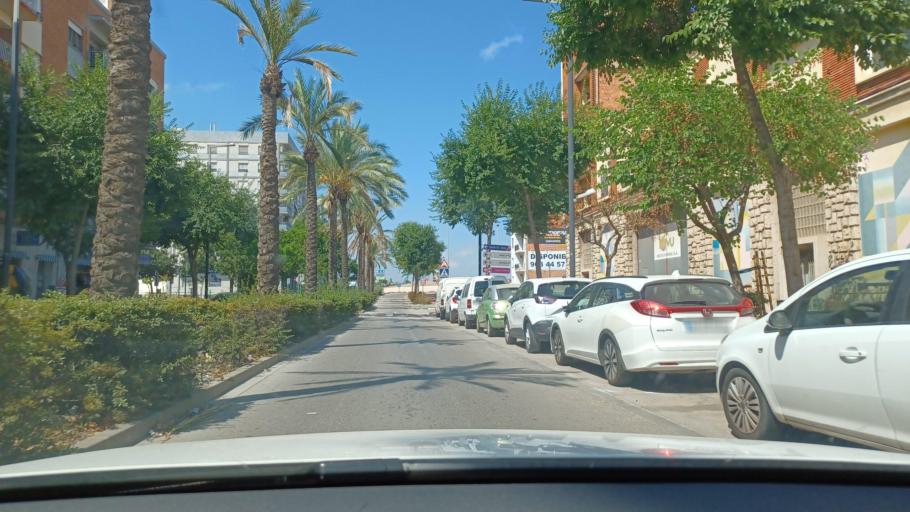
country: ES
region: Valencia
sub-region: Provincia de Valencia
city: Sagunto
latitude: 39.6785
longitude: -0.2705
